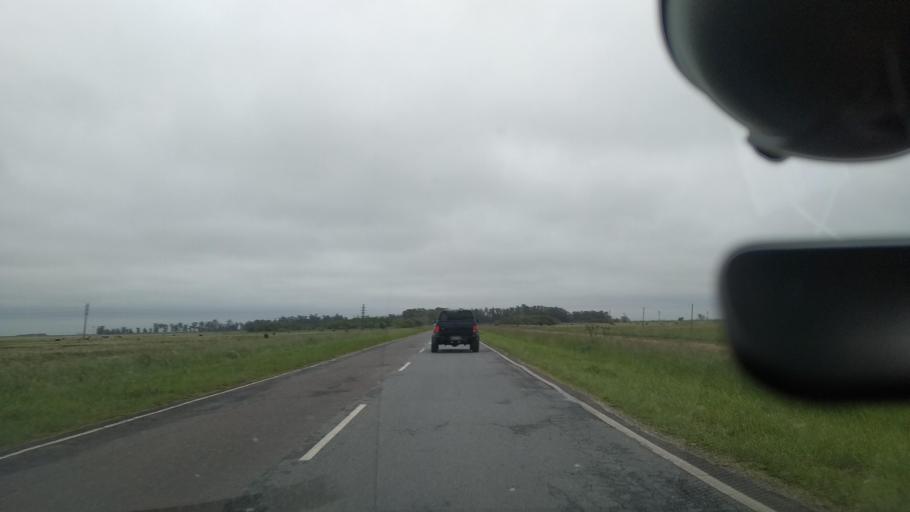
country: AR
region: Buenos Aires
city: Veronica
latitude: -35.5203
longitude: -57.3304
